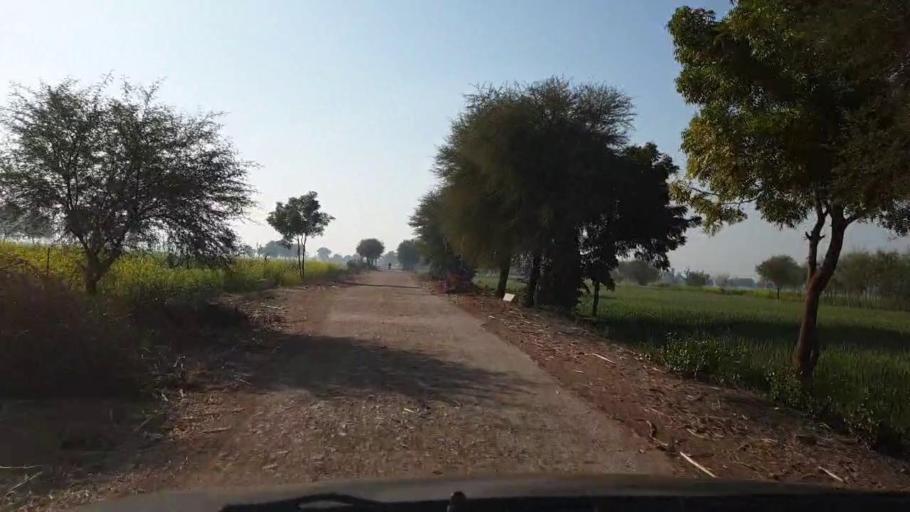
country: PK
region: Sindh
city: Jhol
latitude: 25.9350
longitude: 68.8654
